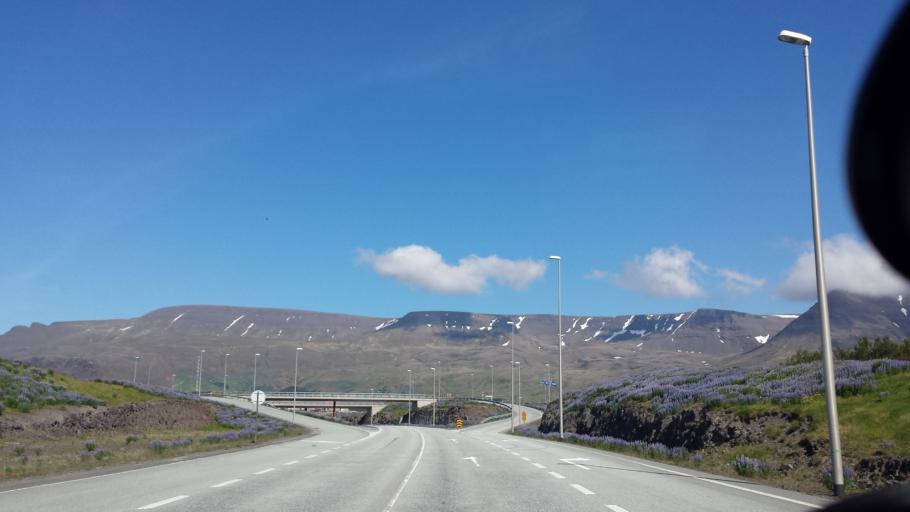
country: IS
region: Capital Region
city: Mosfellsbaer
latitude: 64.1815
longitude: -21.6791
